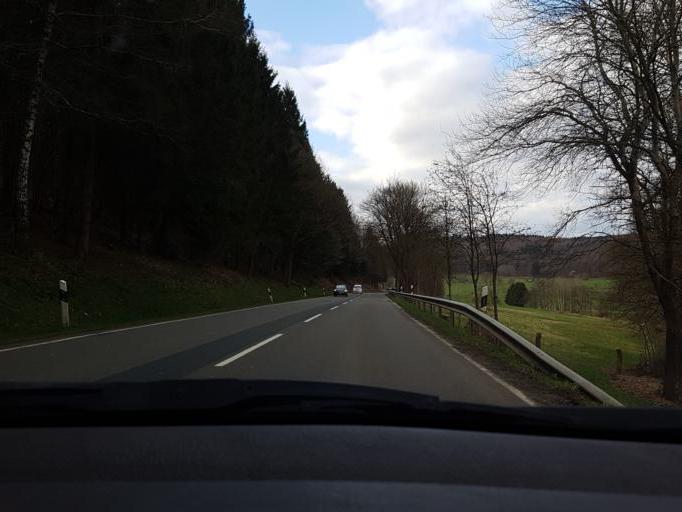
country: DE
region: Lower Saxony
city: Bodenfelde
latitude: 51.7023
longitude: 9.5481
